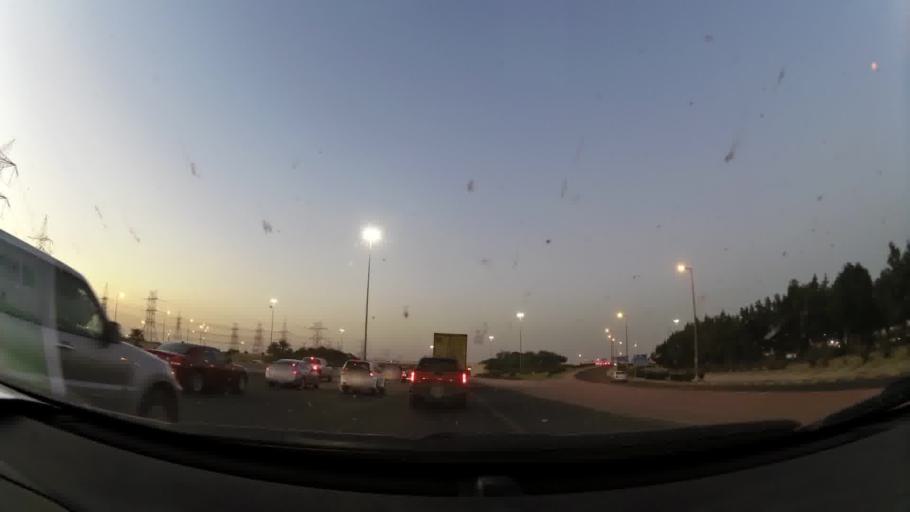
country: KW
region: Mubarak al Kabir
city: Sabah as Salim
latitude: 29.2365
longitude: 48.0510
